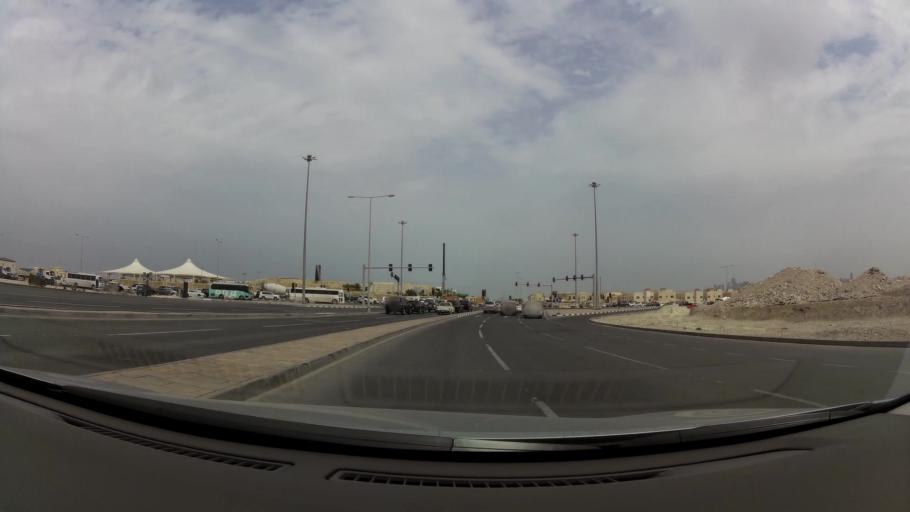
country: QA
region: Baladiyat ar Rayyan
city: Ar Rayyan
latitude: 25.3582
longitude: 51.4765
